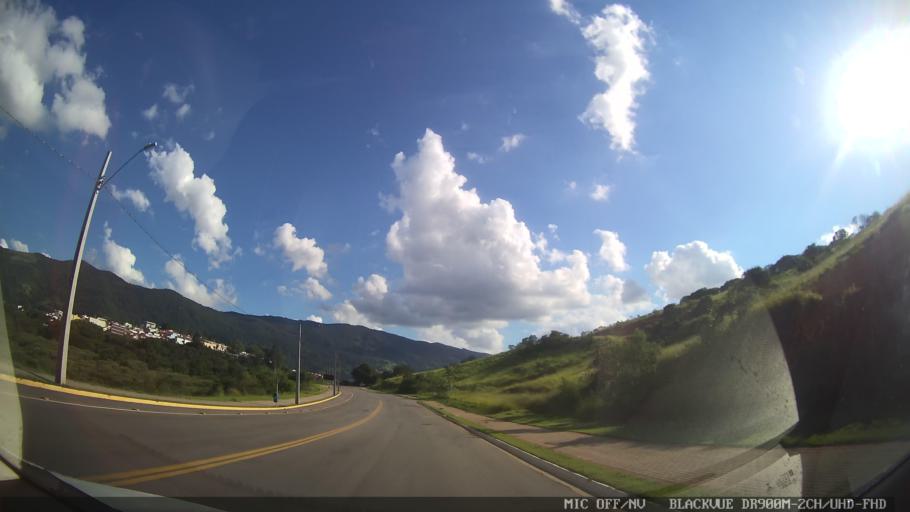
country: BR
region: Minas Gerais
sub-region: Extrema
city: Extrema
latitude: -22.8463
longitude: -46.3239
